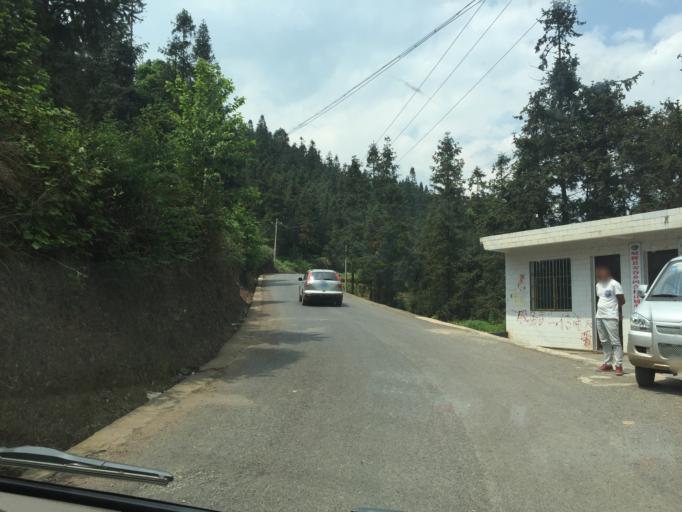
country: CN
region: Guangxi Zhuangzu Zizhiqu
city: Xinzhou
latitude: 25.6966
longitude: 105.2286
